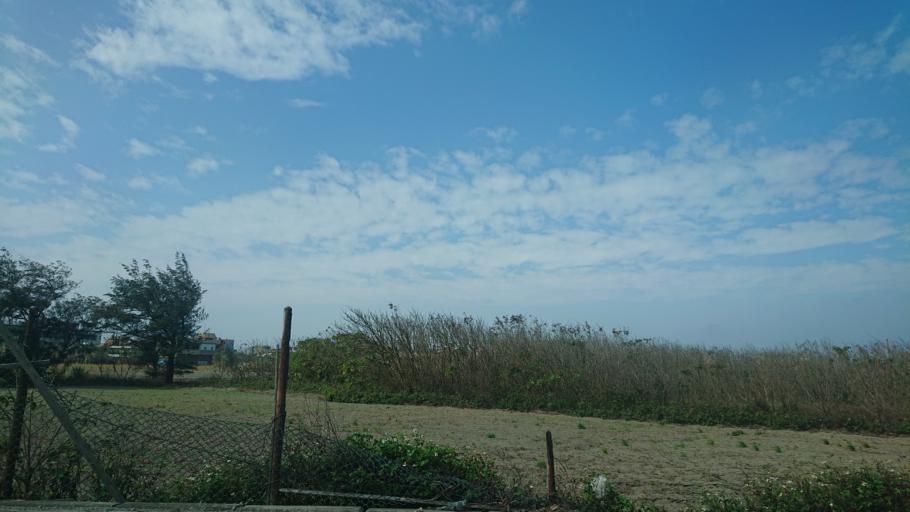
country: TW
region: Taiwan
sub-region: Changhua
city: Chang-hua
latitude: 23.9265
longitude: 120.3225
